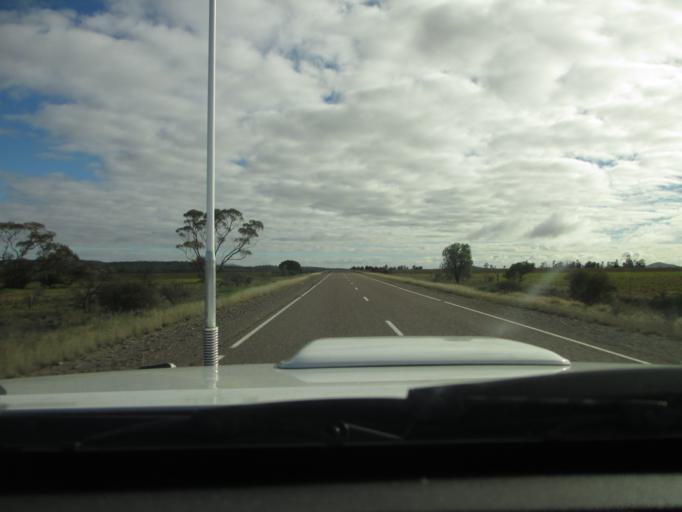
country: AU
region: South Australia
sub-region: Peterborough
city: Peterborough
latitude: -32.5404
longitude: 138.5586
